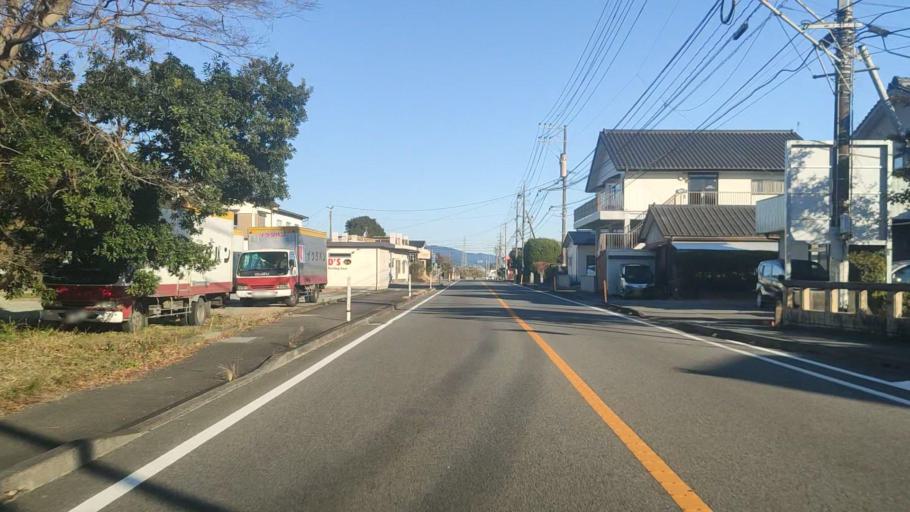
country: JP
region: Miyazaki
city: Nobeoka
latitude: 32.3855
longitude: 131.6275
